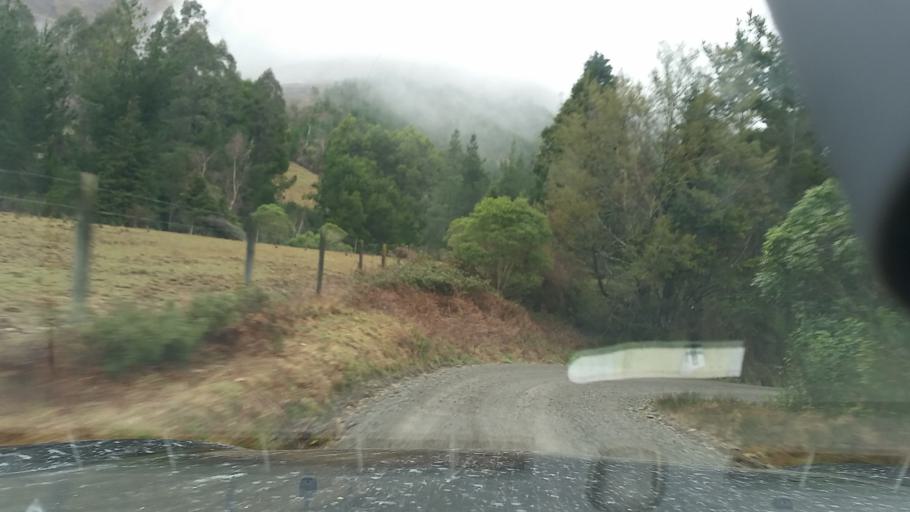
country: NZ
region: Nelson
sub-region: Nelson City
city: Nelson
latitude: -41.3571
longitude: 173.6218
